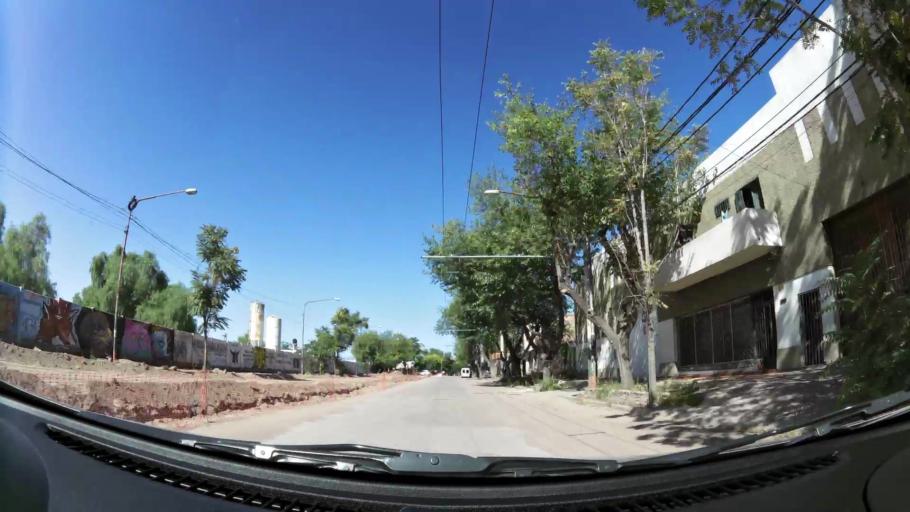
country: AR
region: Mendoza
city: Mendoza
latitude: -32.8895
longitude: -68.8128
